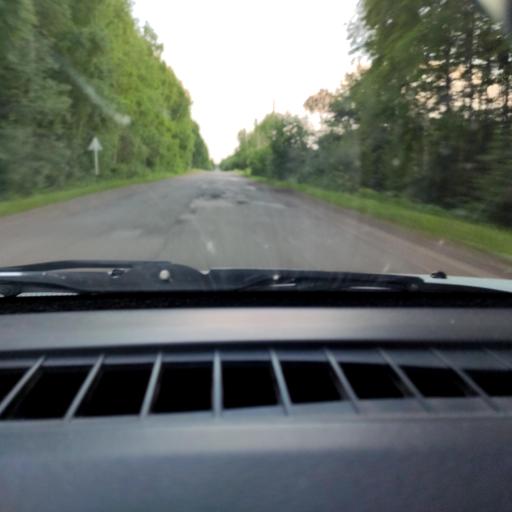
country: RU
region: Perm
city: Uinskoye
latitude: 57.2551
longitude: 56.5329
